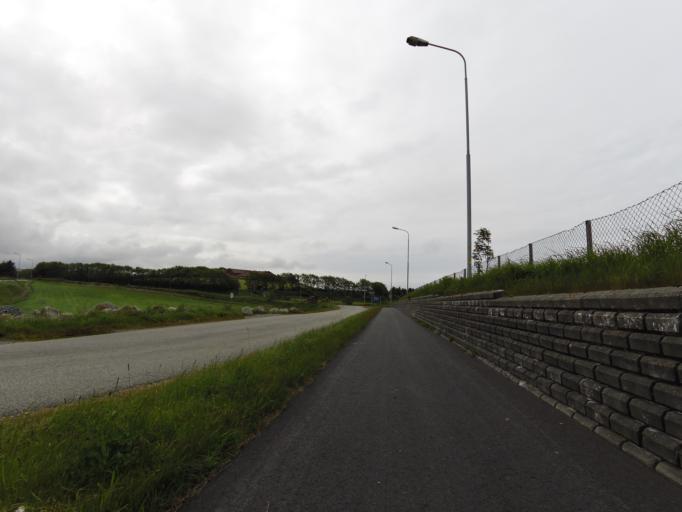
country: NO
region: Rogaland
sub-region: Klepp
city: Kleppe
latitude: 58.8213
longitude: 5.5884
